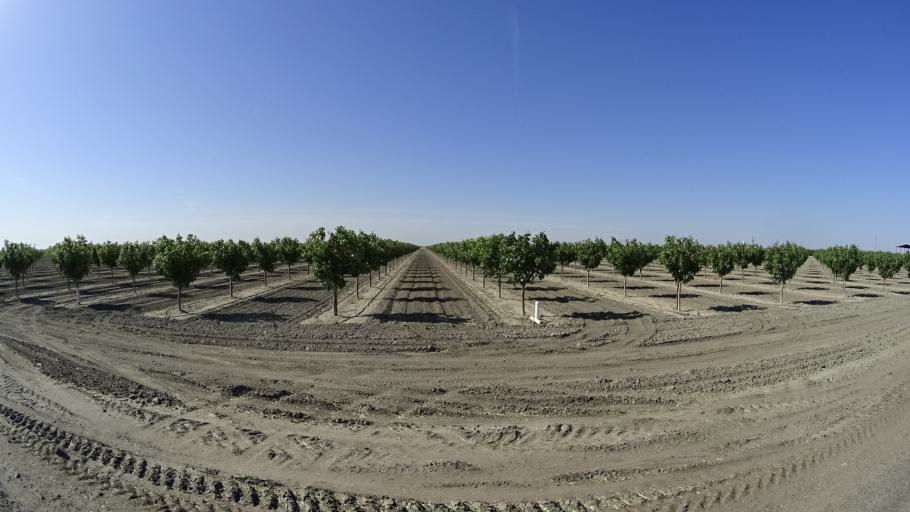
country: US
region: California
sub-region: Kings County
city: Corcoran
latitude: 36.0833
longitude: -119.5885
